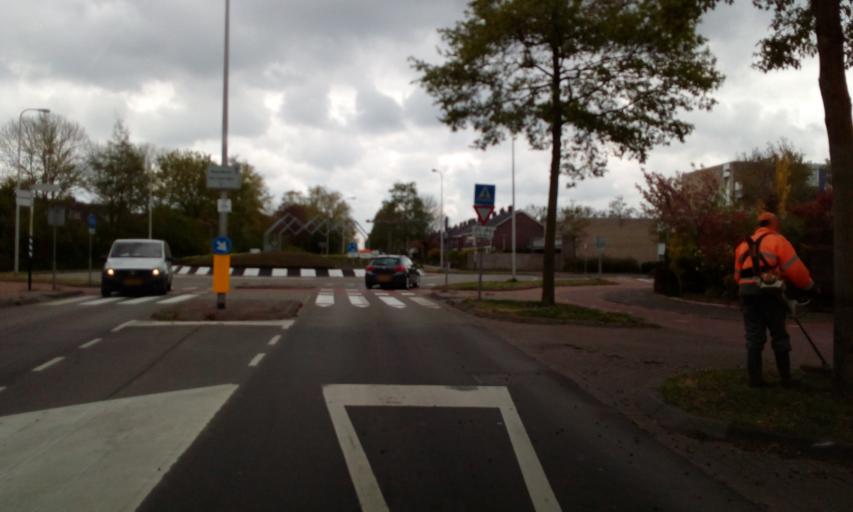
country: NL
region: South Holland
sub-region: Gemeente Barendrecht
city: Barendrecht
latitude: 51.8504
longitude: 4.5363
